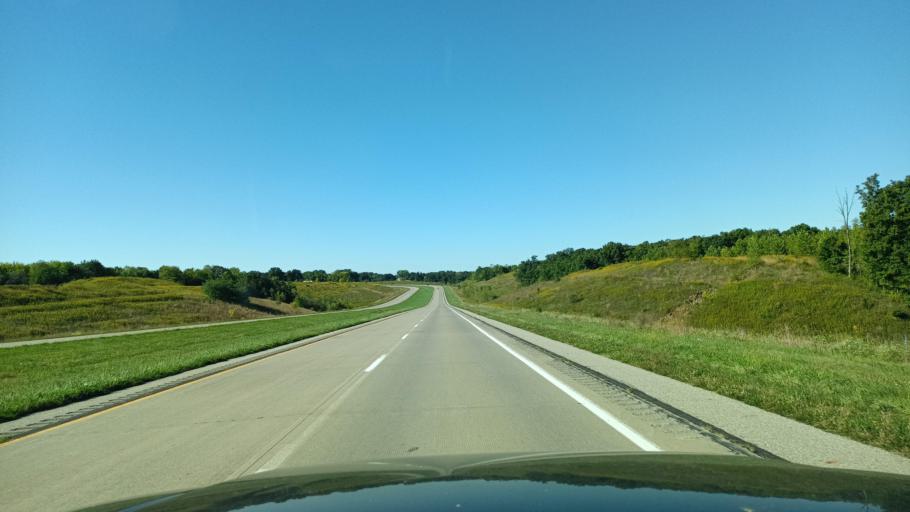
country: US
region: Iowa
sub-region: Lee County
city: Fort Madison
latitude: 40.6479
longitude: -91.3694
